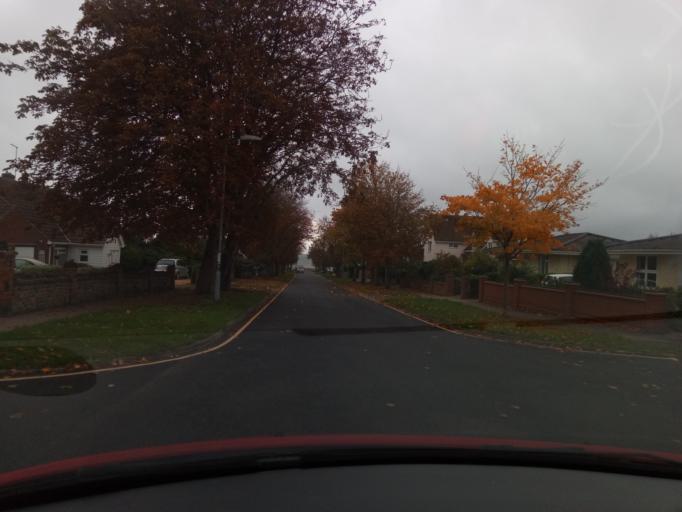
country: GB
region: England
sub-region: Essex
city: West Mersea
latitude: 51.7762
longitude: 0.9318
